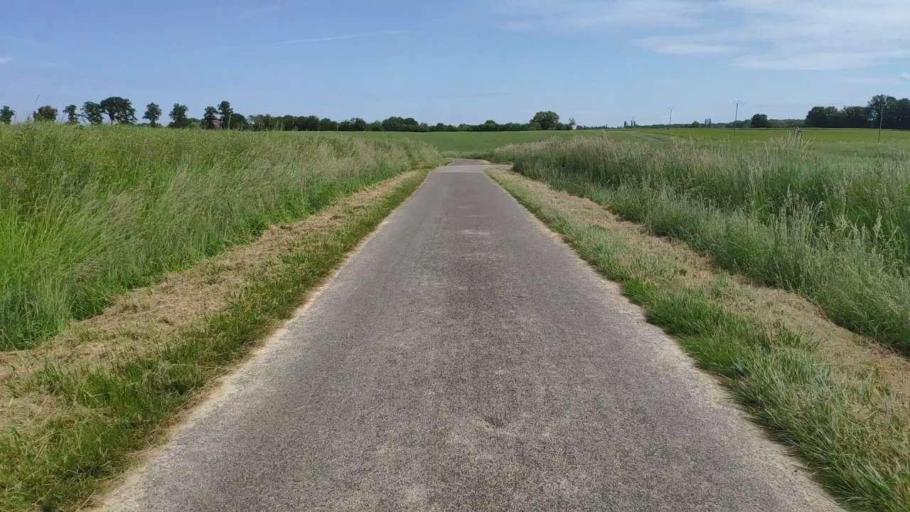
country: FR
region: Franche-Comte
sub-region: Departement du Jura
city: Bletterans
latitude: 46.6851
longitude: 5.4094
